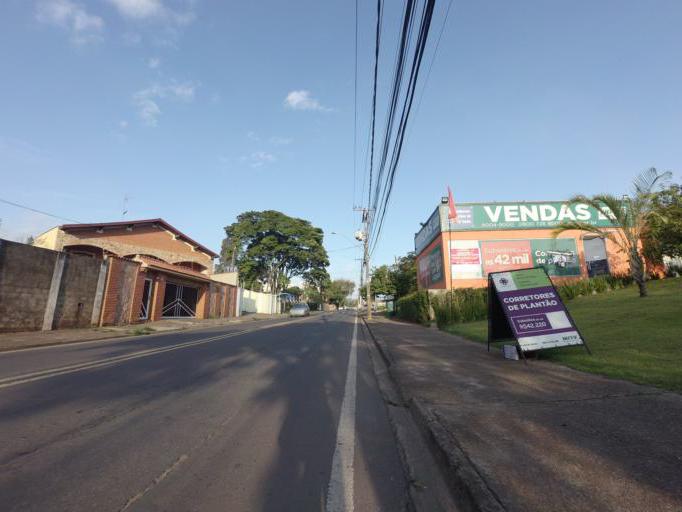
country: BR
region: Sao Paulo
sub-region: Piracicaba
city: Piracicaba
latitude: -22.7419
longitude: -47.6041
